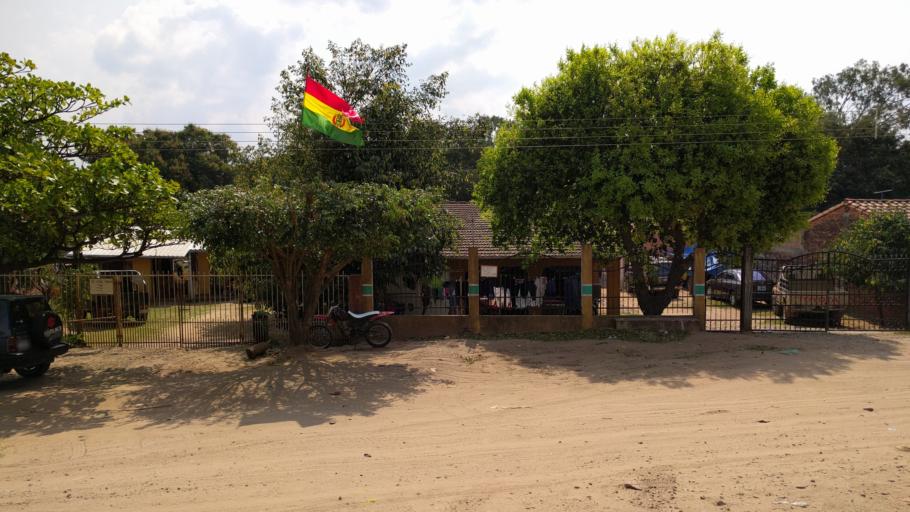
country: BO
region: Santa Cruz
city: Santa Rita
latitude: -17.8945
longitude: -63.3366
